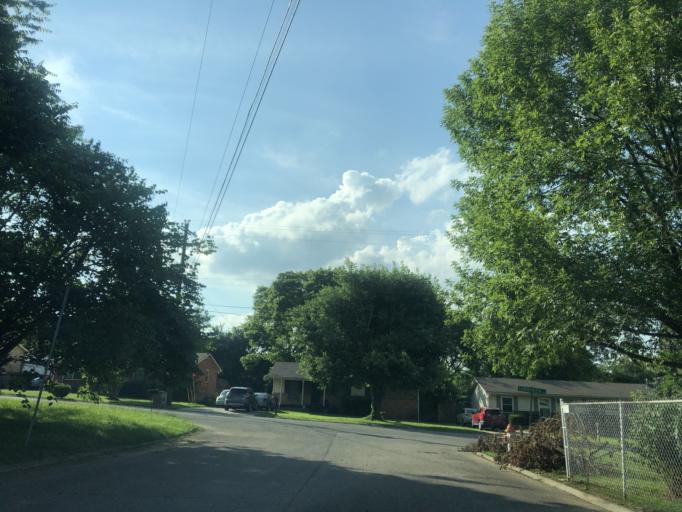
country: US
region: Tennessee
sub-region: Davidson County
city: Nashville
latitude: 36.2290
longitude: -86.8291
